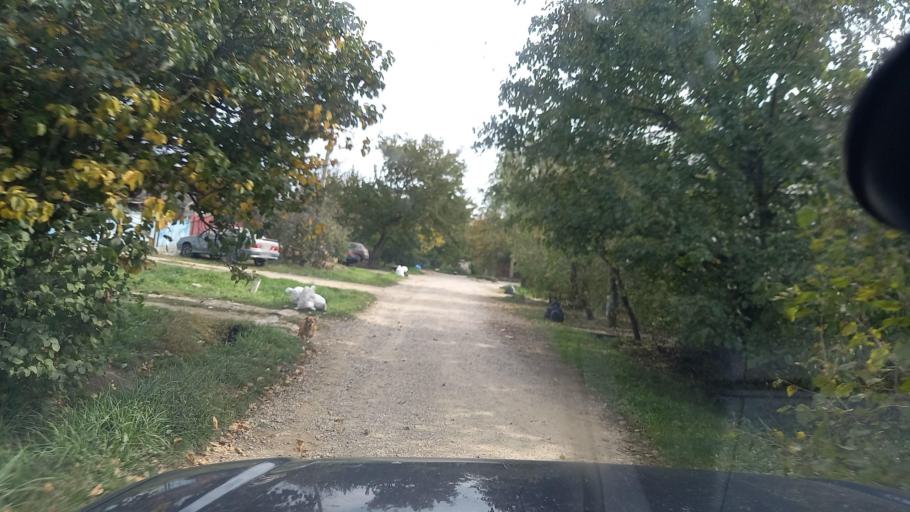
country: RU
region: Krasnodarskiy
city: Il'skiy
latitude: 44.8488
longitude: 38.5623
